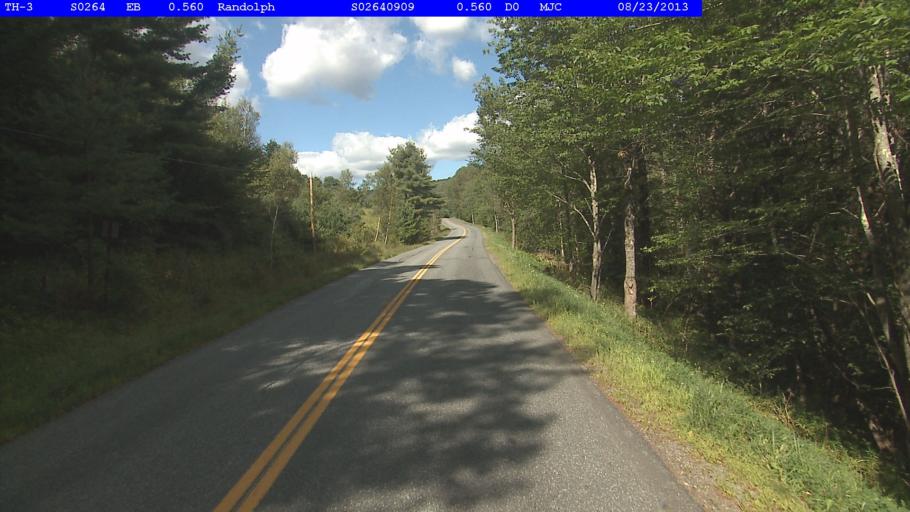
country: US
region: Vermont
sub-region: Orange County
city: Chelsea
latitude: 43.9380
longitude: -72.5439
